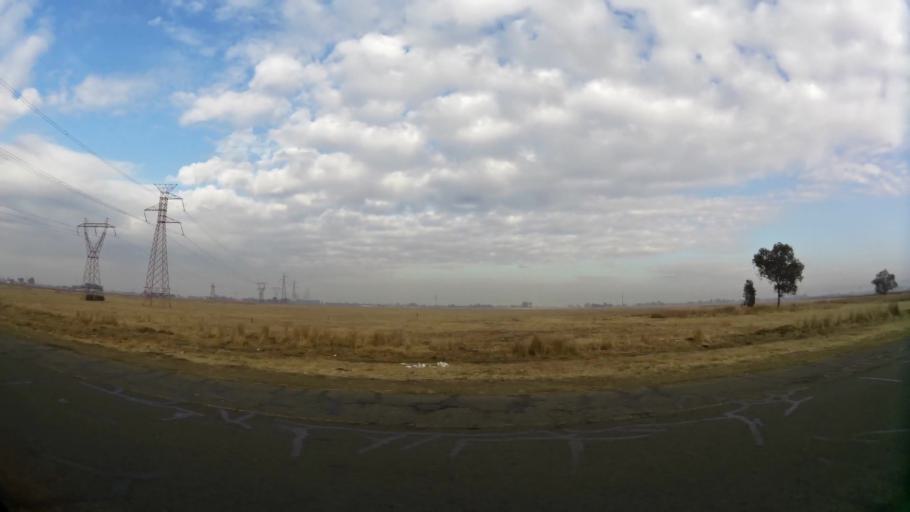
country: ZA
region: Gauteng
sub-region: Sedibeng District Municipality
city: Vanderbijlpark
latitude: -26.6662
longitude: 27.7874
